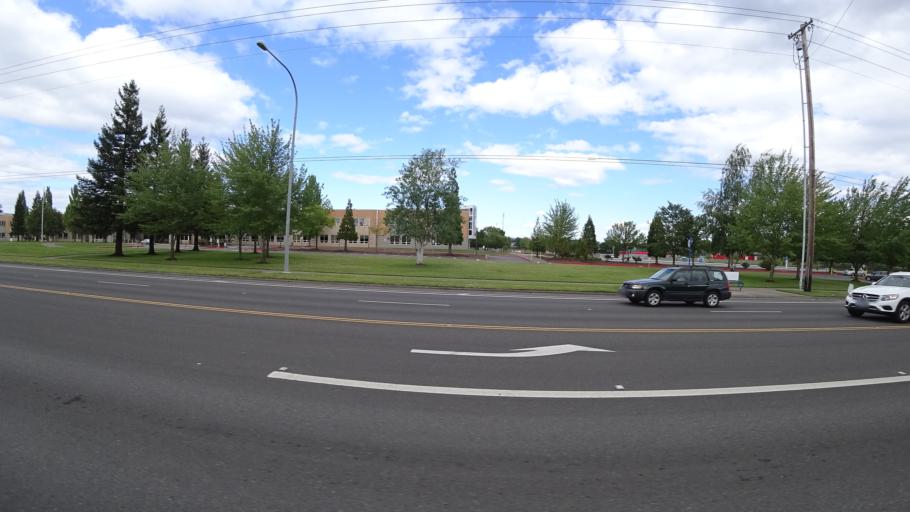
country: US
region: Oregon
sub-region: Washington County
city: Bethany
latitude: 45.5496
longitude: -122.8676
